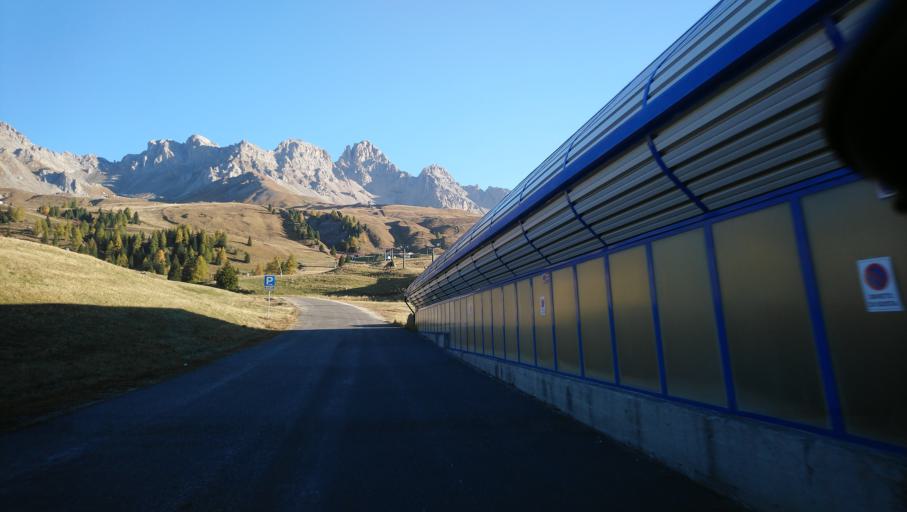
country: IT
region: Veneto
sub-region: Provincia di Belluno
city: Falcade Alto
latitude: 46.3792
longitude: 11.7942
